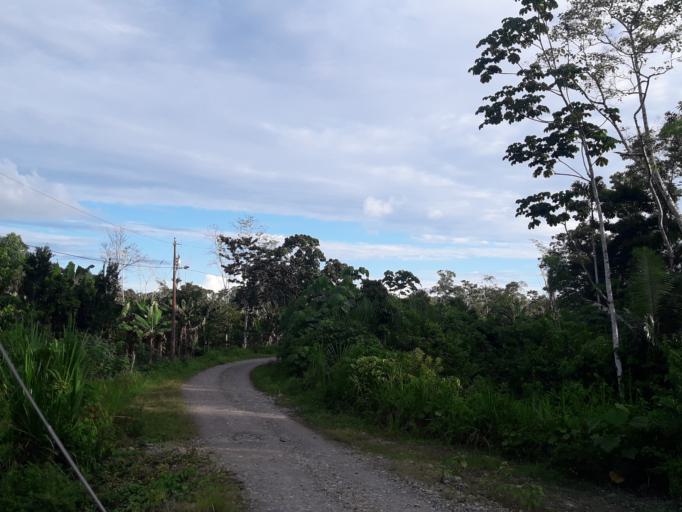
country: EC
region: Orellana
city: Boca Suno
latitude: -0.8994
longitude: -77.3093
